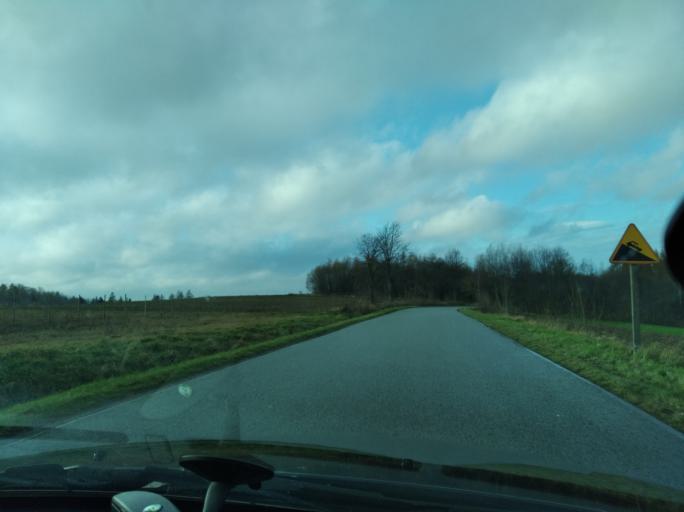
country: PL
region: Subcarpathian Voivodeship
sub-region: Powiat ropczycko-sedziszowski
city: Wielopole Skrzynskie
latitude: 49.9384
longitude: 21.6826
